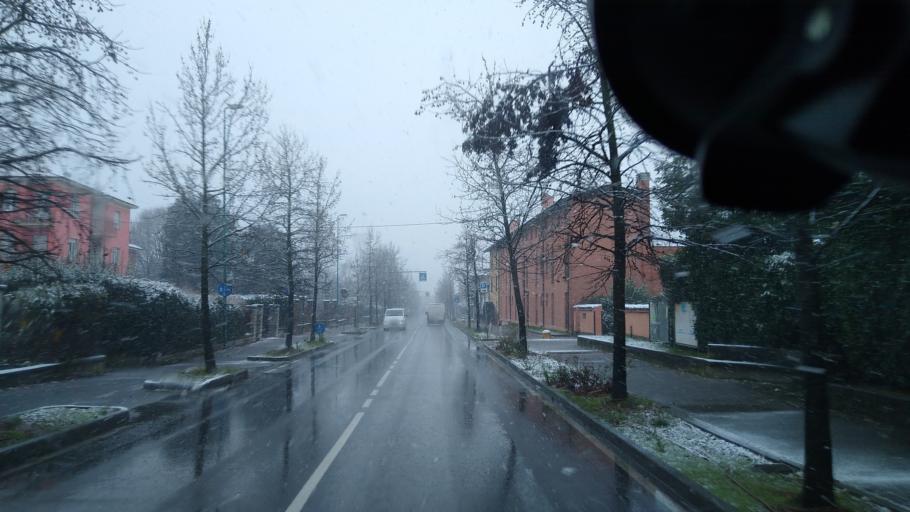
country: IT
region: Lombardy
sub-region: Provincia di Bergamo
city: Bariano
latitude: 45.5169
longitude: 9.7048
